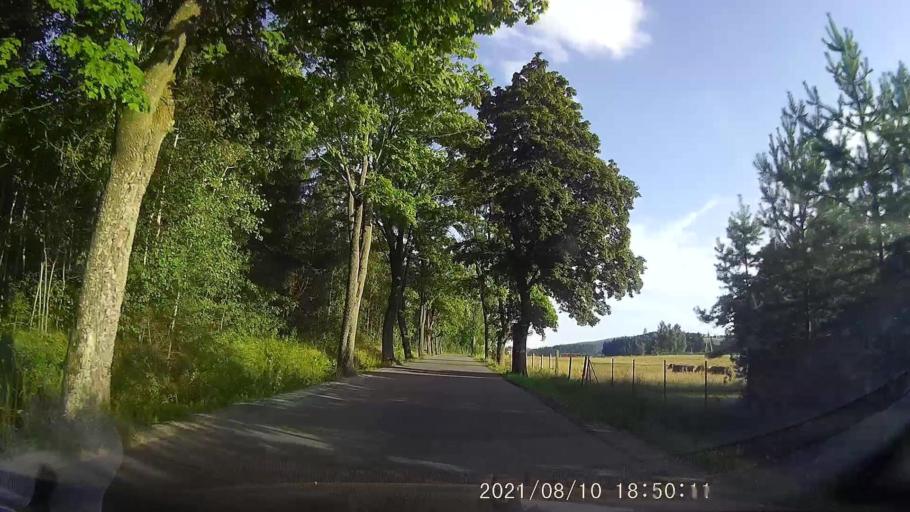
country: PL
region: Lower Silesian Voivodeship
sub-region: Powiat klodzki
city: Duszniki-Zdroj
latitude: 50.4211
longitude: 16.3760
